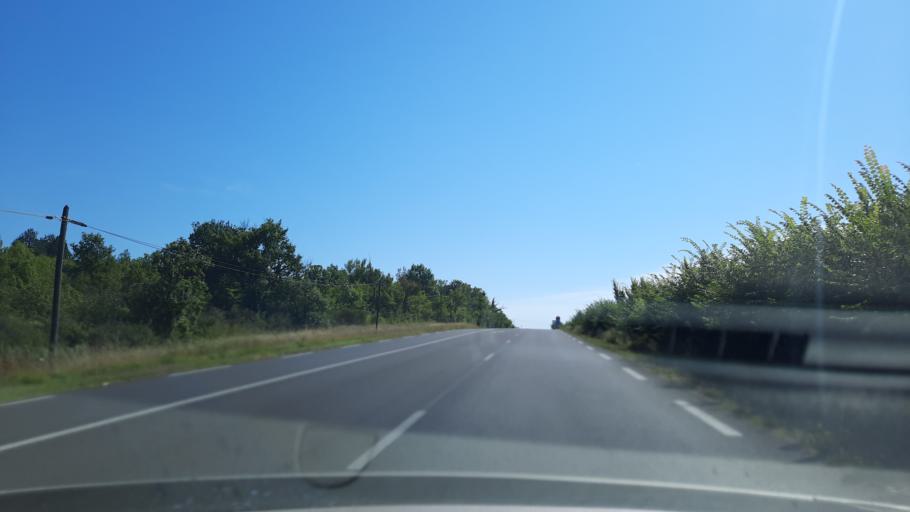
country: FR
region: Midi-Pyrenees
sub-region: Departement du Tarn-et-Garonne
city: Septfonds
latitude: 44.1906
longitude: 1.6709
